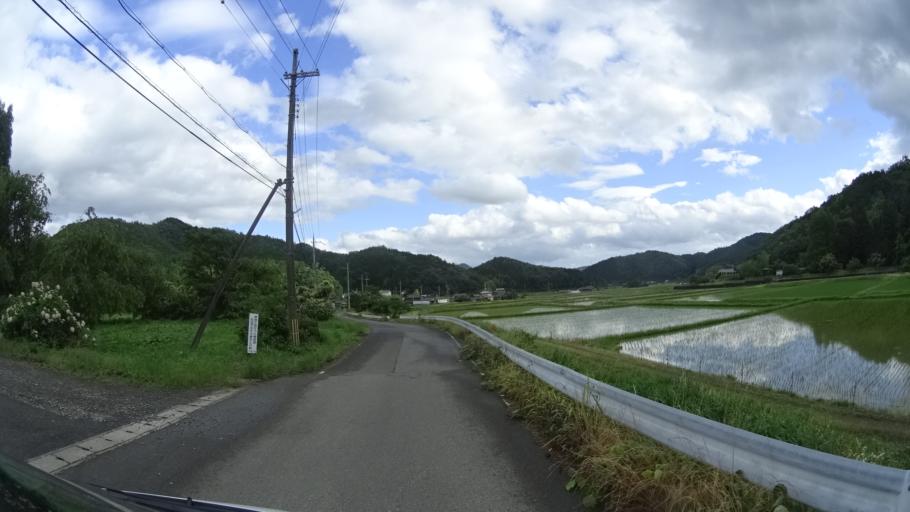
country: JP
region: Kyoto
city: Ayabe
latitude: 35.3849
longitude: 135.2384
